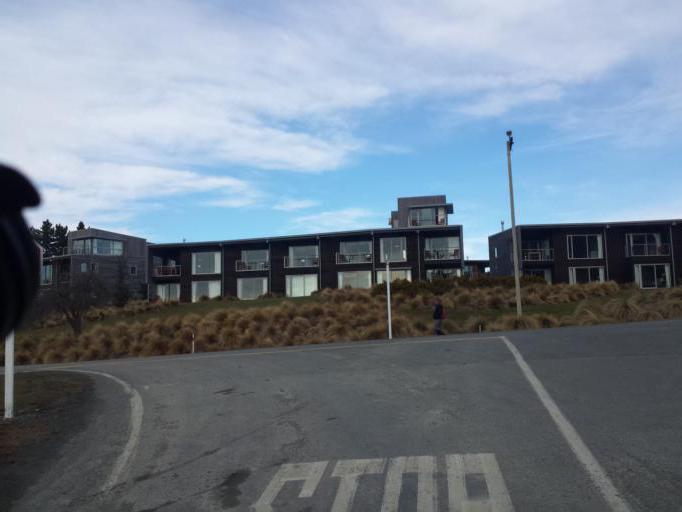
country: NZ
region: Canterbury
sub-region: Timaru District
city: Pleasant Point
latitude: -44.0029
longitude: 170.4737
